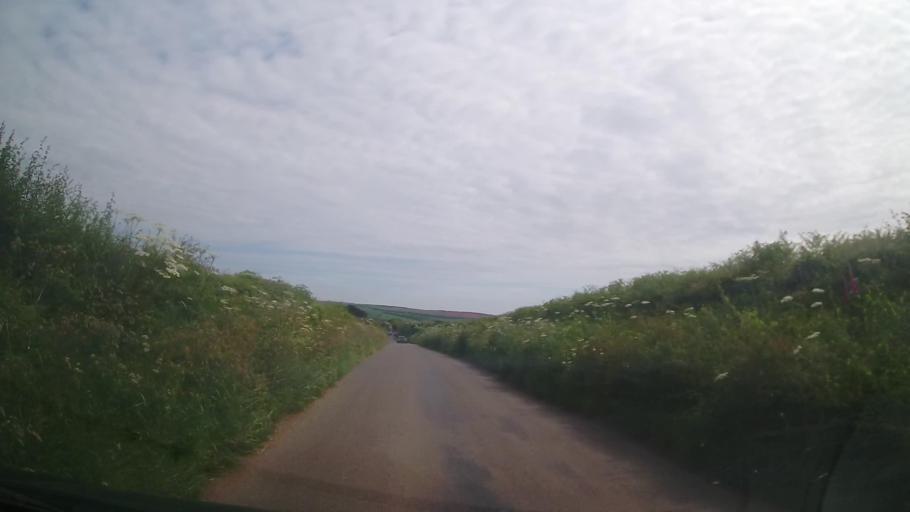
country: GB
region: England
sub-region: Devon
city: Salcombe
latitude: 50.2462
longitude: -3.6821
